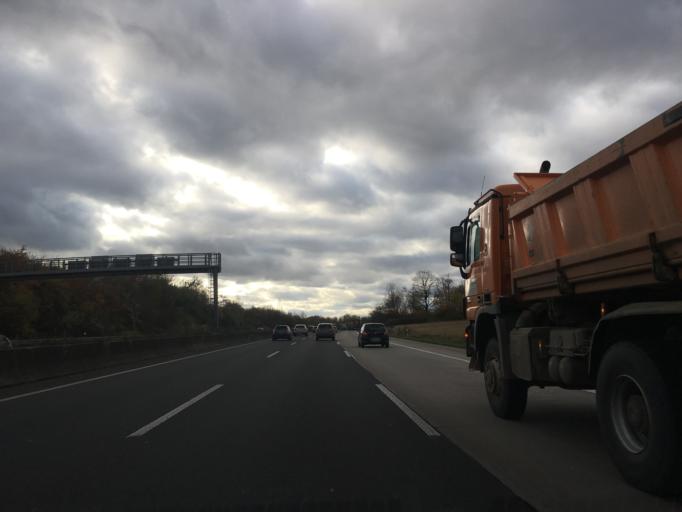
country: DE
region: North Rhine-Westphalia
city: Tuernich
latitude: 50.9121
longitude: 6.7393
